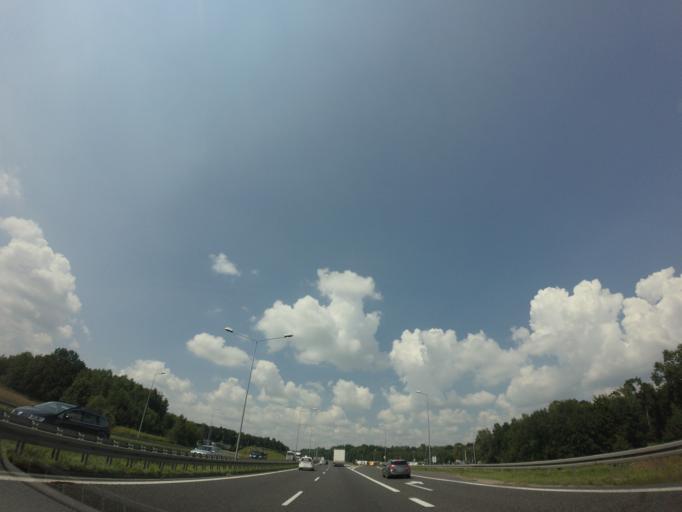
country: PL
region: Opole Voivodeship
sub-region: Powiat strzelecki
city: Ujazd
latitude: 50.4233
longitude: 18.3940
